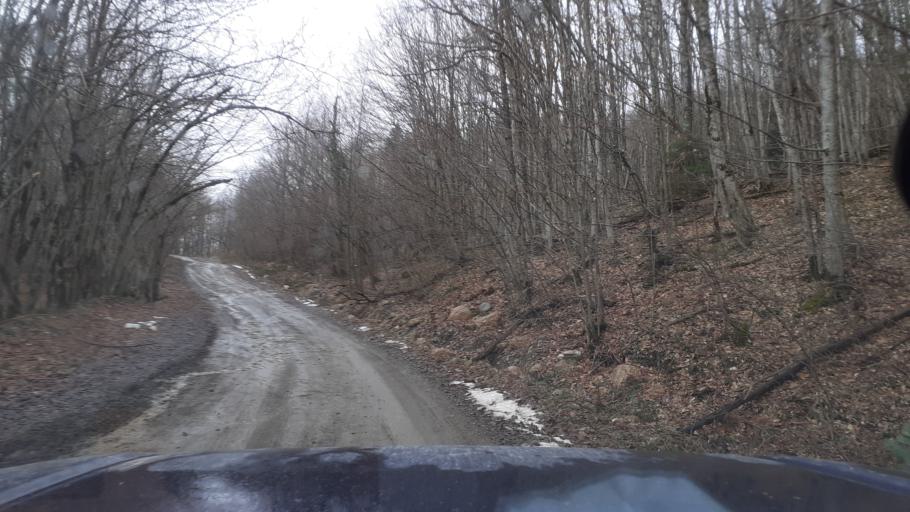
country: RU
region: Krasnodarskiy
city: Neftegorsk
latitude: 44.0687
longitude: 39.7293
